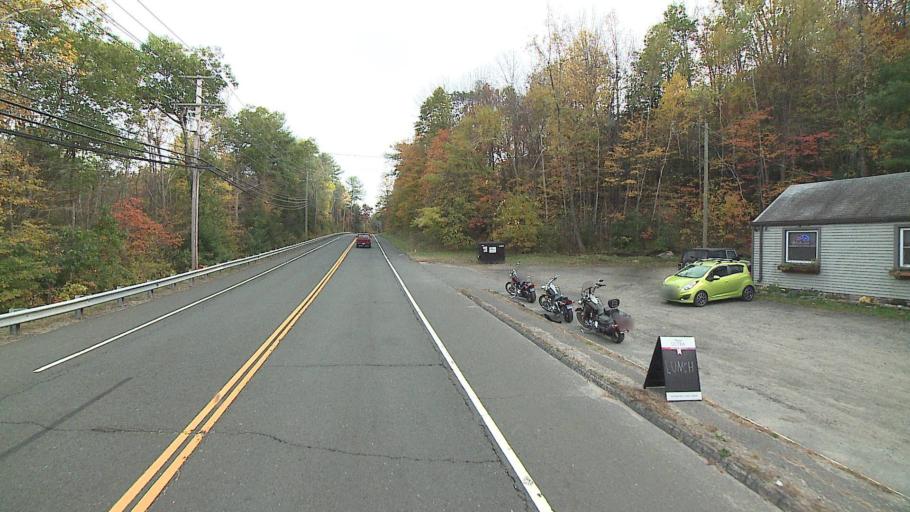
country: US
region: Connecticut
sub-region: Litchfield County
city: New Hartford Center
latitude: 41.9021
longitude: -72.9947
